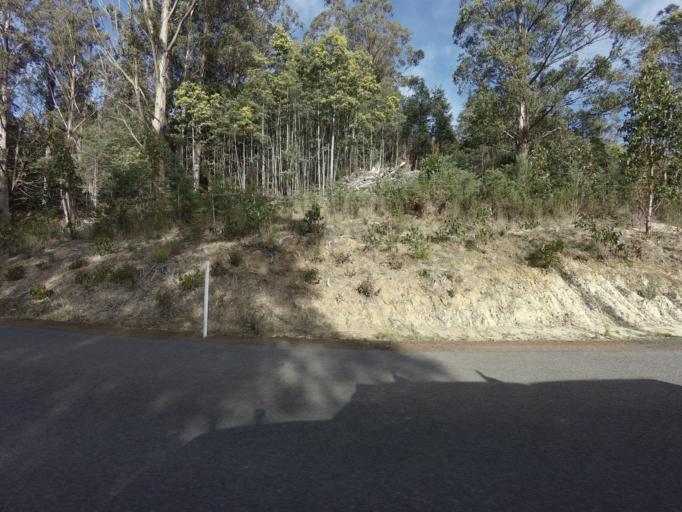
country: AU
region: Tasmania
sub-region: Kingborough
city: Margate
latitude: -43.0143
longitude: 147.1606
